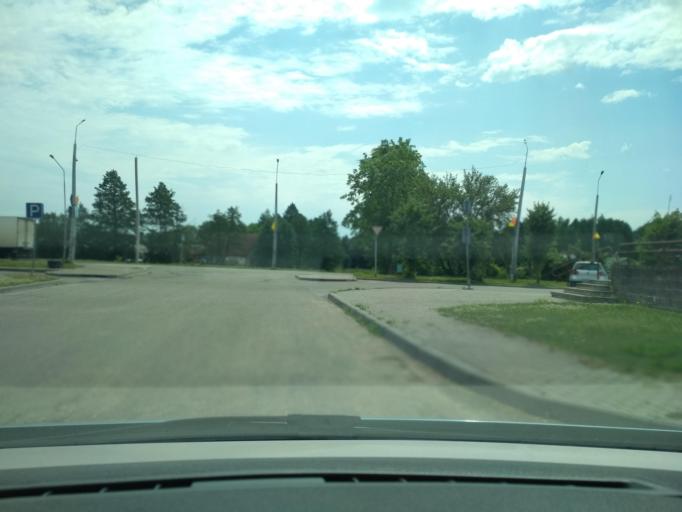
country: BY
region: Grodnenskaya
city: Astravyets
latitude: 54.6142
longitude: 25.9514
